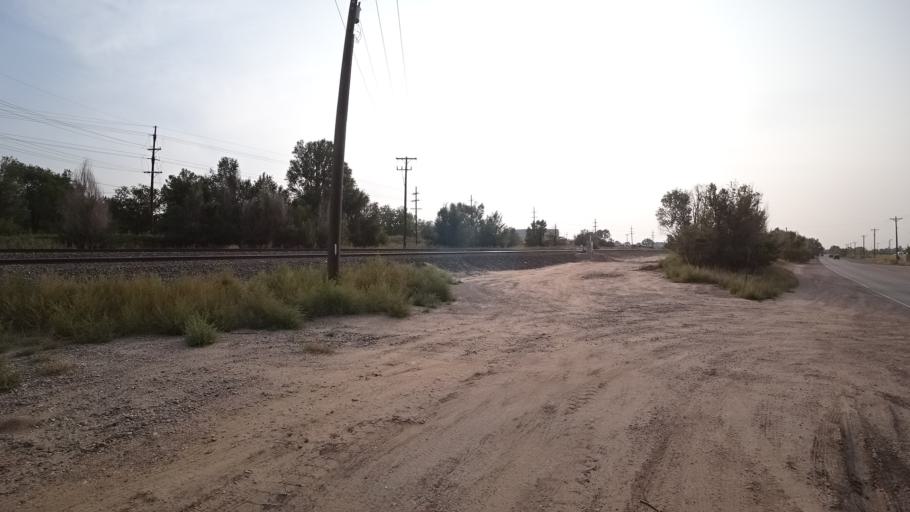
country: US
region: Colorado
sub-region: El Paso County
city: Stratmoor
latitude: 38.7972
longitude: -104.7839
